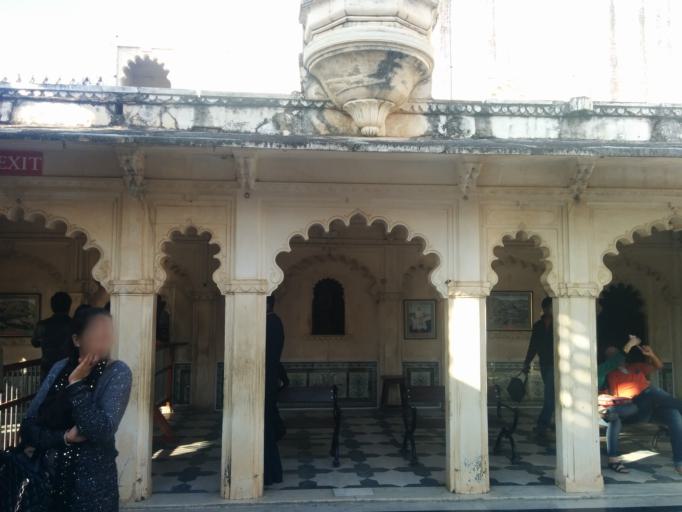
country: IN
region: Rajasthan
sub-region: Udaipur
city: Udaipur
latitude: 24.5768
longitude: 73.6835
